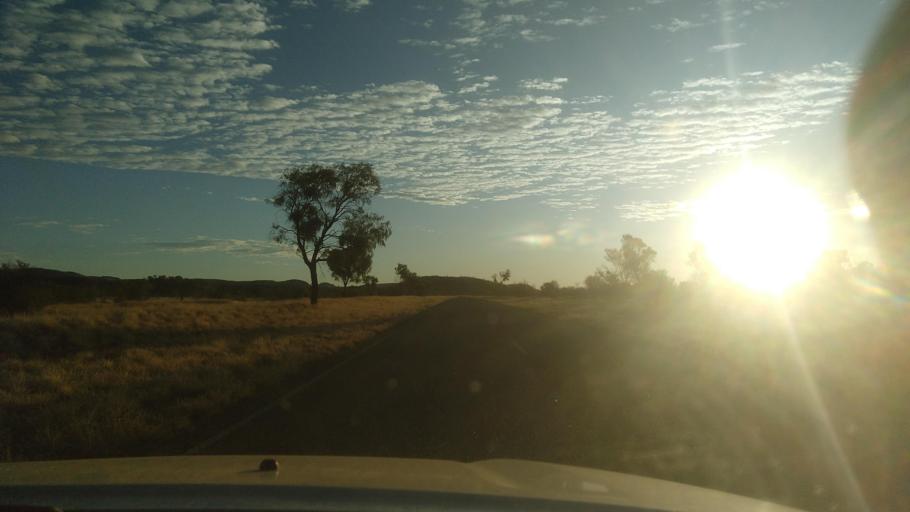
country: AU
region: Northern Territory
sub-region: Alice Springs
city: Alice Springs
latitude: -23.7191
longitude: 133.7532
